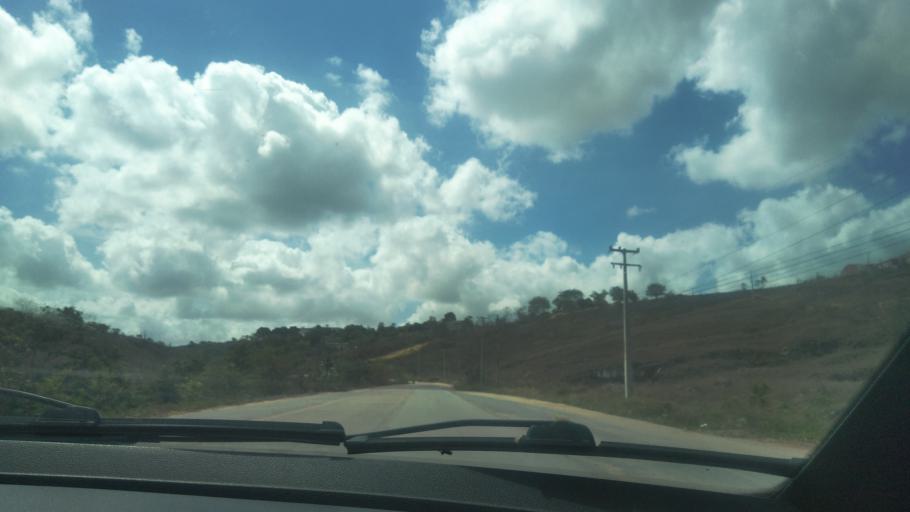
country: BR
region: Pernambuco
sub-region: Vitoria De Santo Antao
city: Vitoria de Santo Antao
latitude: -8.1311
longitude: -35.2821
